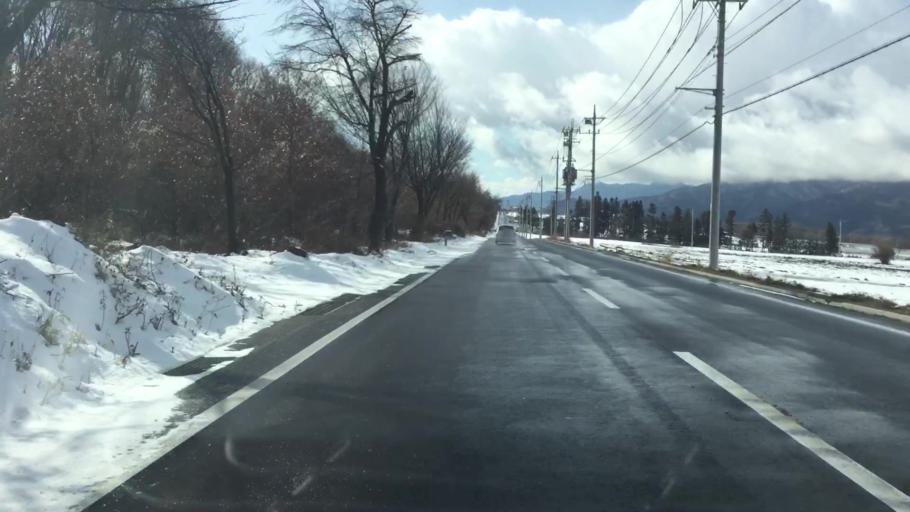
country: JP
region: Gunma
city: Numata
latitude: 36.6209
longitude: 139.0870
